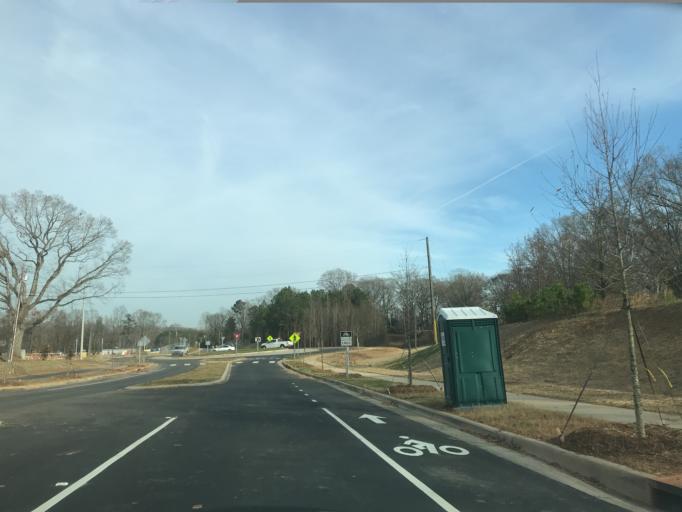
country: US
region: North Carolina
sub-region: Wake County
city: West Raleigh
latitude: 35.7765
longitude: -78.6680
